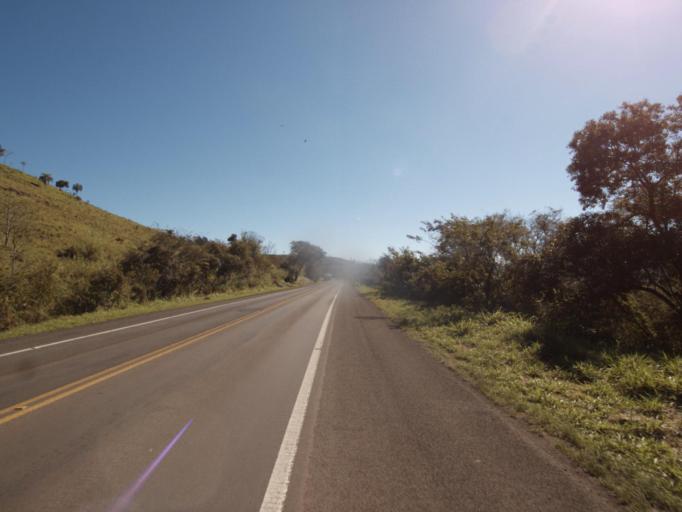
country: BR
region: Rio Grande do Sul
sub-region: Frederico Westphalen
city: Frederico Westphalen
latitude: -26.8242
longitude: -53.4067
